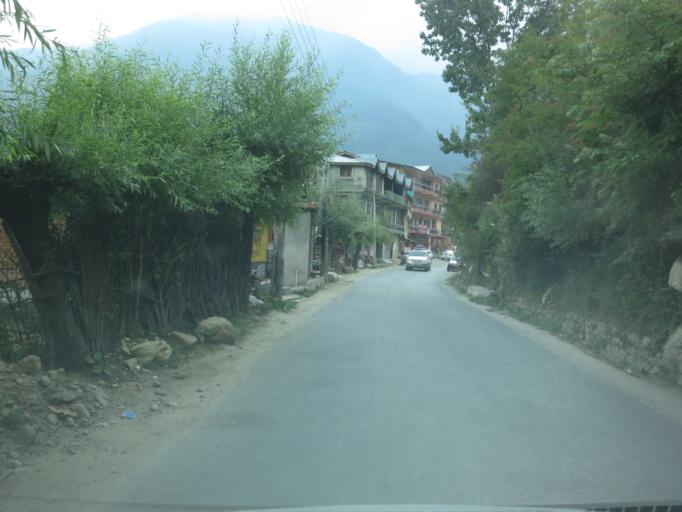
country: IN
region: Himachal Pradesh
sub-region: Kulu
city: Manali
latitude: 32.2203
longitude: 77.1980
